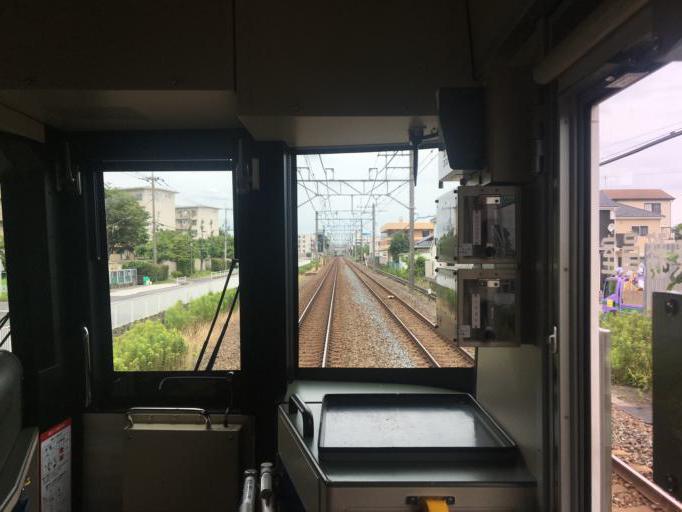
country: JP
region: Saitama
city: Kasukabe
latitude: 35.9436
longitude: 139.7722
